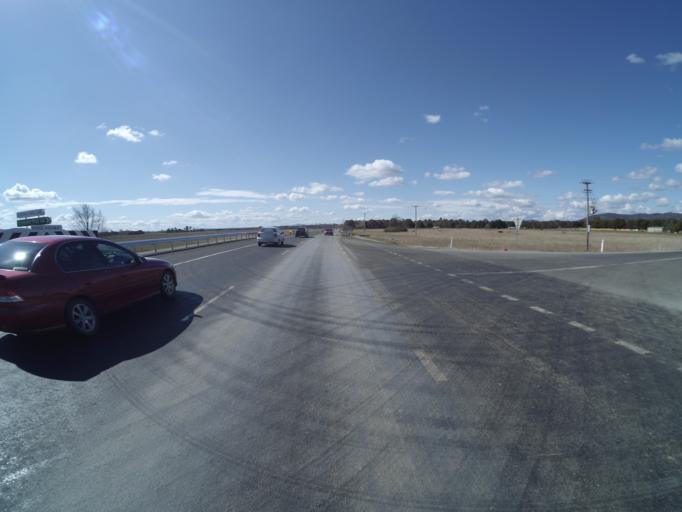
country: AU
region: New South Wales
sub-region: Palerang
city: Bungendore
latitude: -35.2673
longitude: 149.4314
